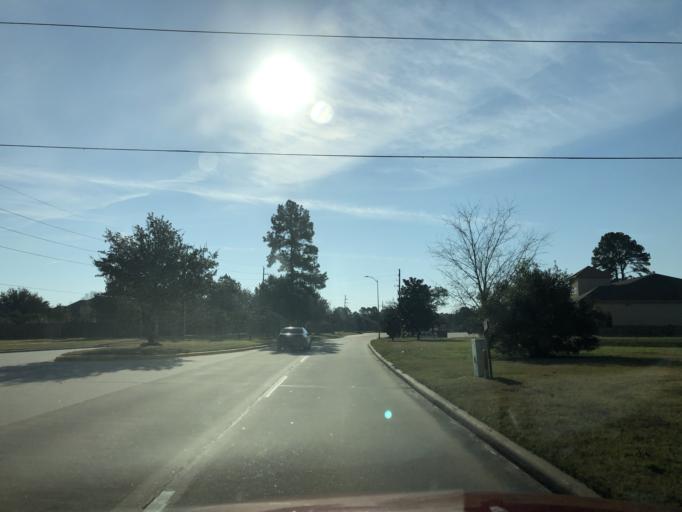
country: US
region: Texas
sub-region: Harris County
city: Tomball
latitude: 30.0484
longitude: -95.5646
